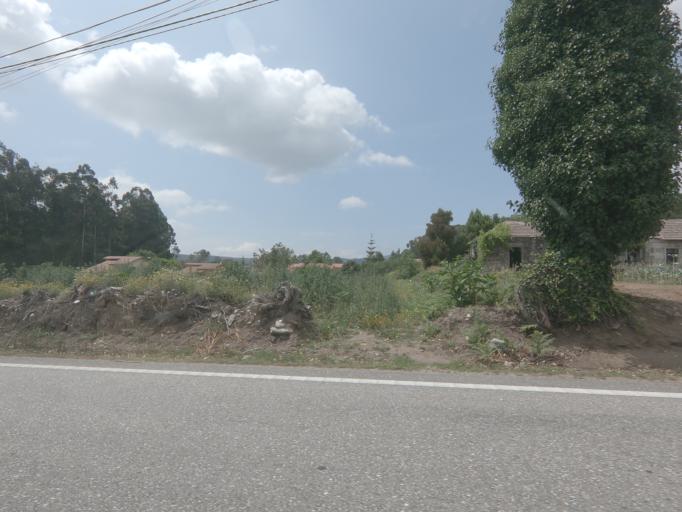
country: PT
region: Viana do Castelo
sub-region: Valenca
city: Valenca
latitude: 42.0256
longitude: -8.6783
